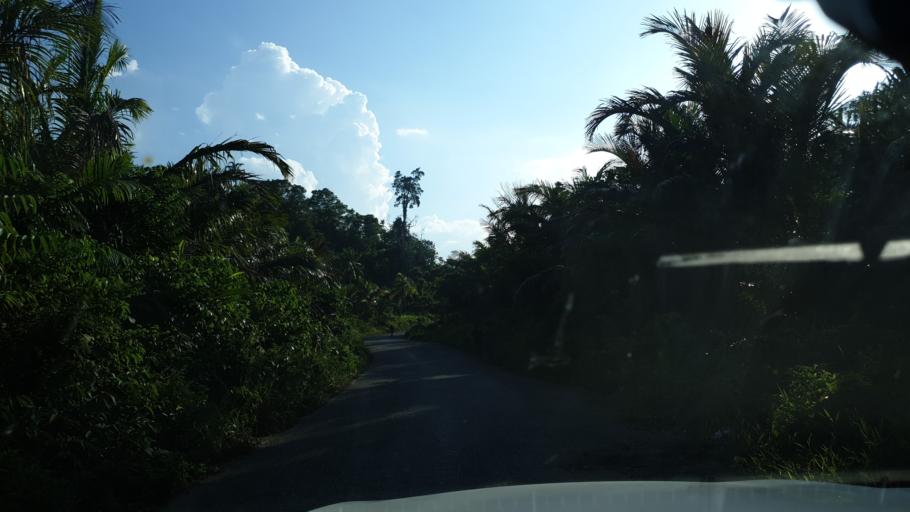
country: PG
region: East Sepik
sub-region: Wewak
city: Wewak
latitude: -3.6918
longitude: 143.6545
